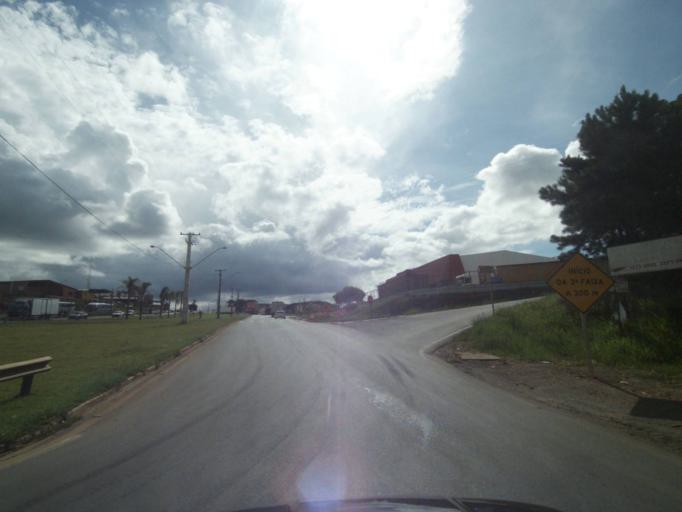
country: BR
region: Parana
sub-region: Telemaco Borba
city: Telemaco Borba
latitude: -24.3299
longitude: -50.6438
